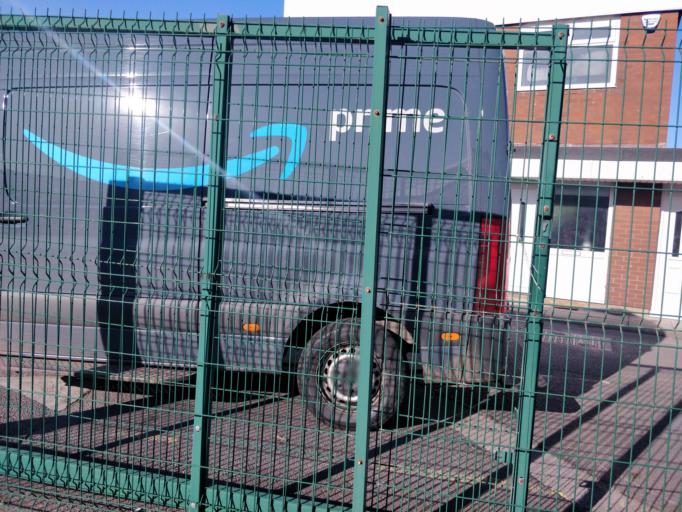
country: GB
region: England
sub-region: Sefton
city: Southport
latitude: 53.6661
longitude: -2.9626
